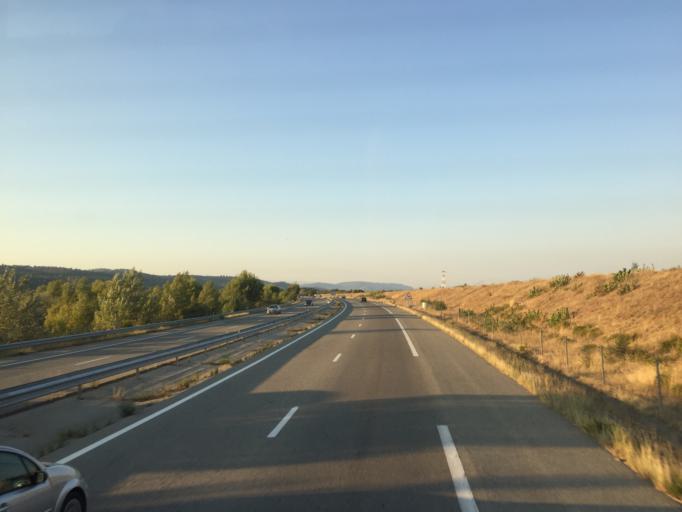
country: FR
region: Provence-Alpes-Cote d'Azur
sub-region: Departement du Vaucluse
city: Beaumont-de-Pertuis
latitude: 43.7099
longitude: 5.7350
